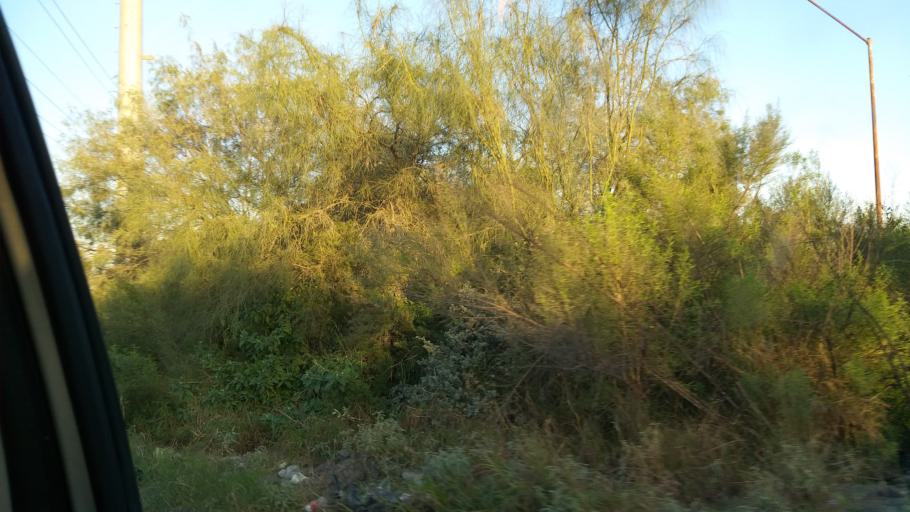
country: MX
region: Nuevo Leon
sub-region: Garcia
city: Parque Industrial Ciudad Mitras
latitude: 25.7799
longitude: -100.4492
